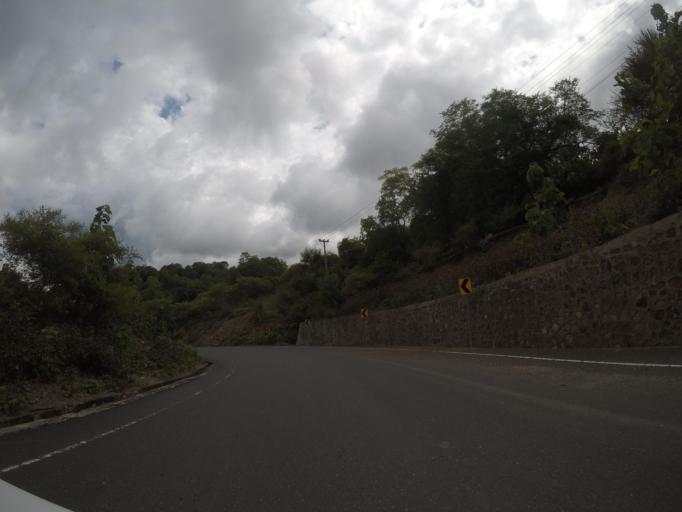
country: TL
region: Liquica
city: Maubara
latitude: -8.7444
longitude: 125.1284
